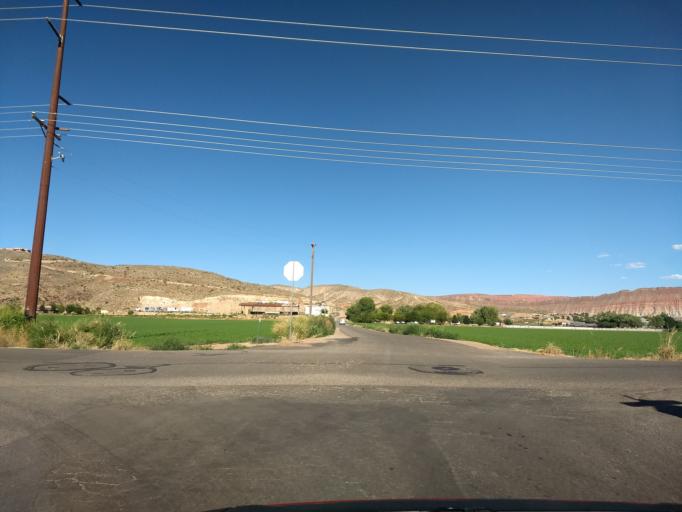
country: US
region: Utah
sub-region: Washington County
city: Washington
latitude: 37.0959
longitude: -113.5093
